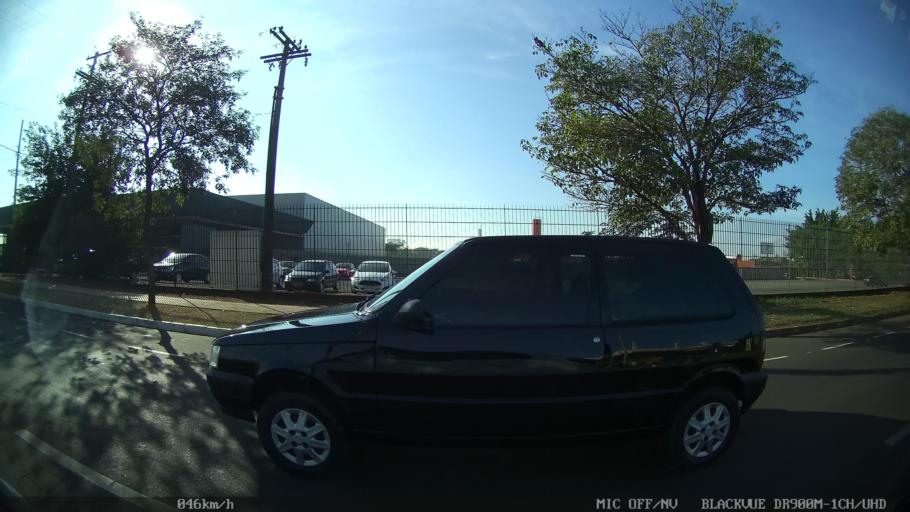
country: BR
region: Sao Paulo
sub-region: Sao Jose Do Rio Preto
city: Sao Jose do Rio Preto
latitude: -20.8001
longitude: -49.3456
